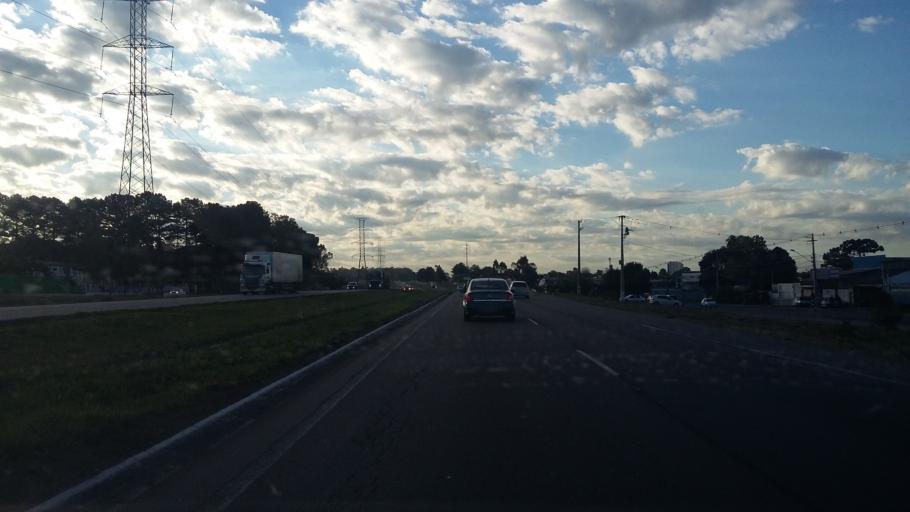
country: BR
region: Parana
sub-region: Curitiba
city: Curitiba
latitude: -25.4778
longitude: -49.3504
